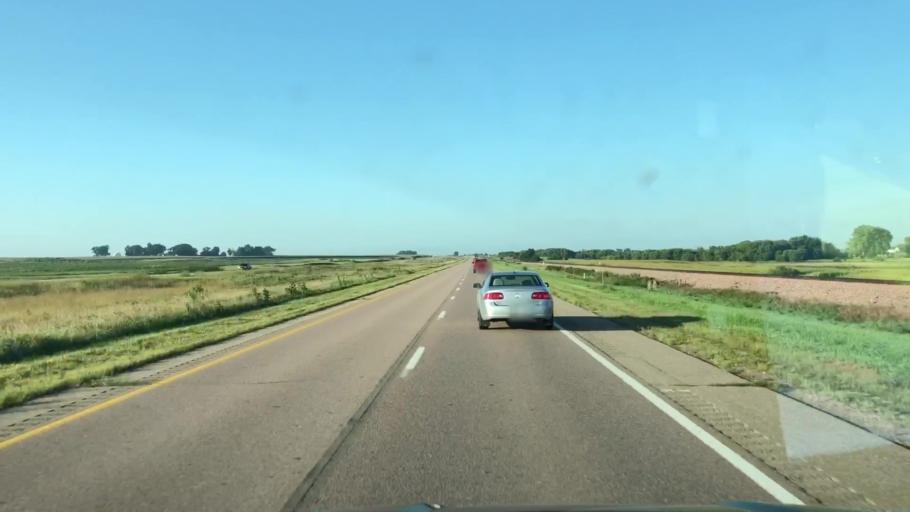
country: US
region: Iowa
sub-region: O'Brien County
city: Sheldon
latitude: 43.1240
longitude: -95.8876
